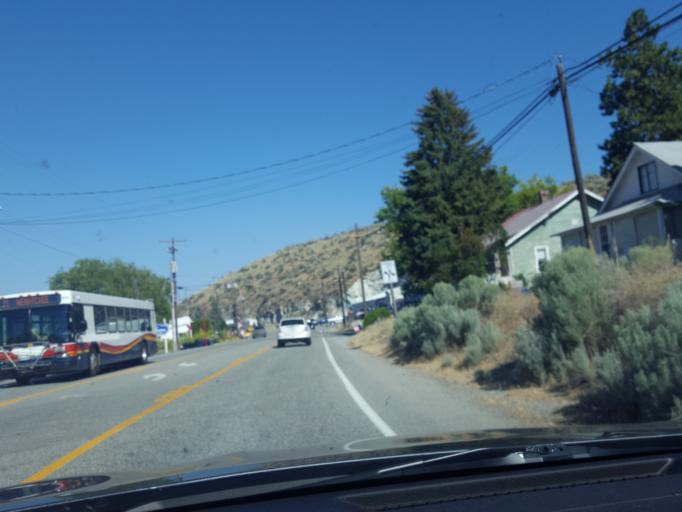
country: US
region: Washington
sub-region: Chelan County
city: Chelan
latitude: 47.8359
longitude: -120.0367
